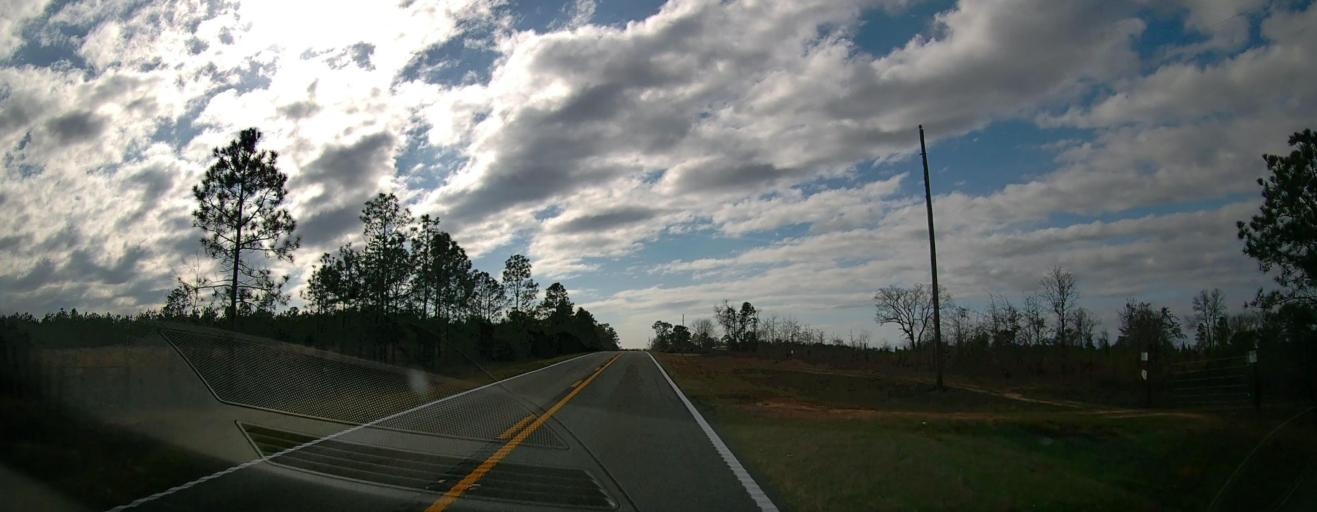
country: US
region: Georgia
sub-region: Marion County
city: Buena Vista
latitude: 32.4448
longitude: -84.5293
